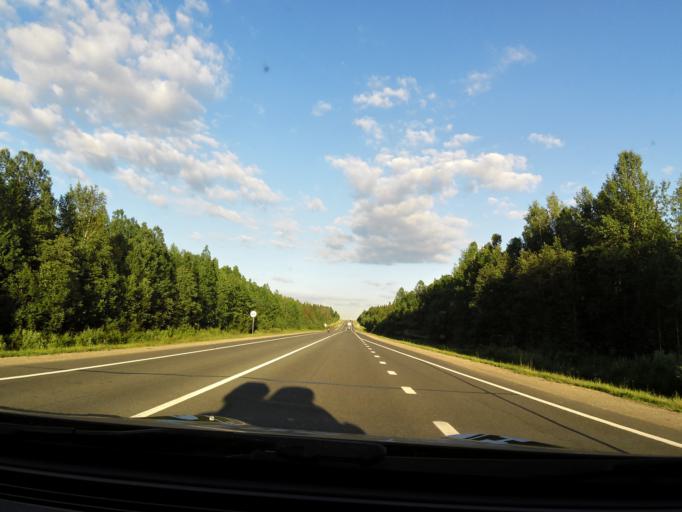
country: RU
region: Vologda
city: Vologda
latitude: 59.0687
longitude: 40.0368
